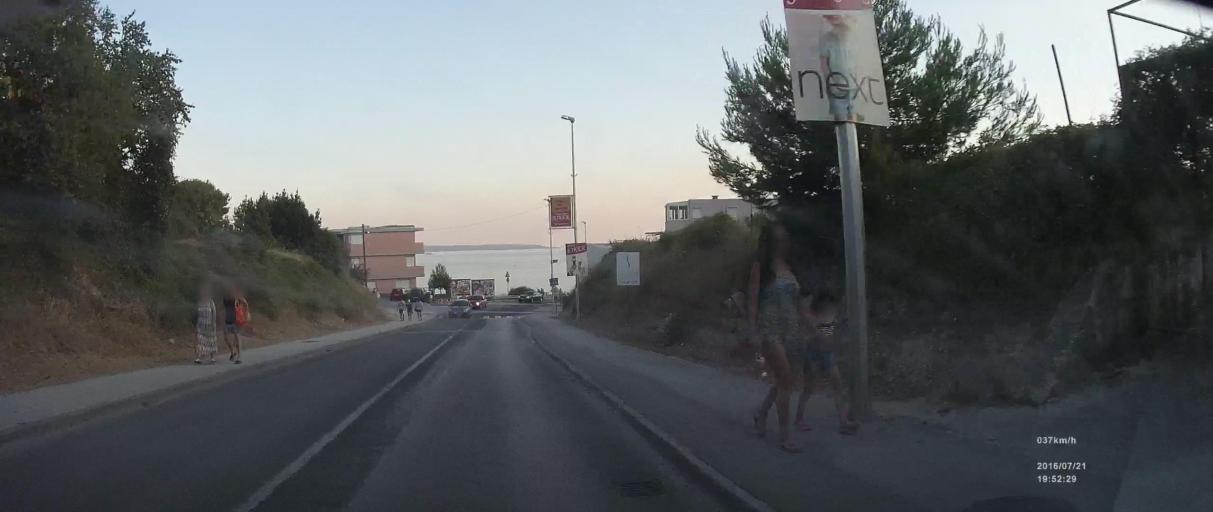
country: HR
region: Splitsko-Dalmatinska
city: Vranjic
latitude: 43.5049
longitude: 16.4780
